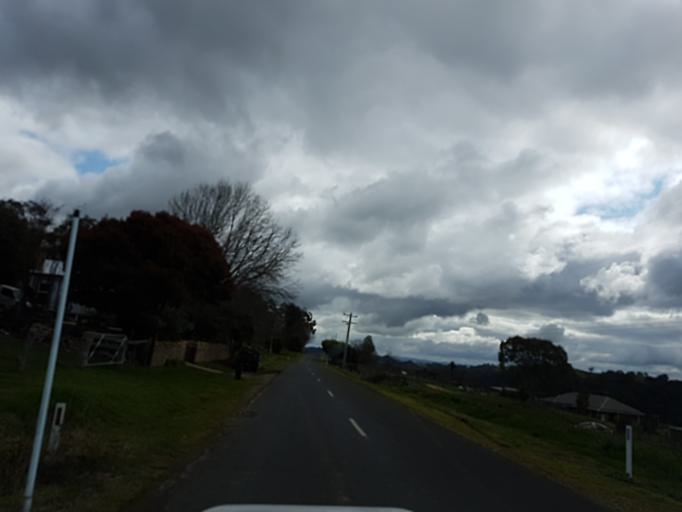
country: AU
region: Victoria
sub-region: Murrindindi
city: Alexandra
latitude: -37.3031
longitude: 145.8434
